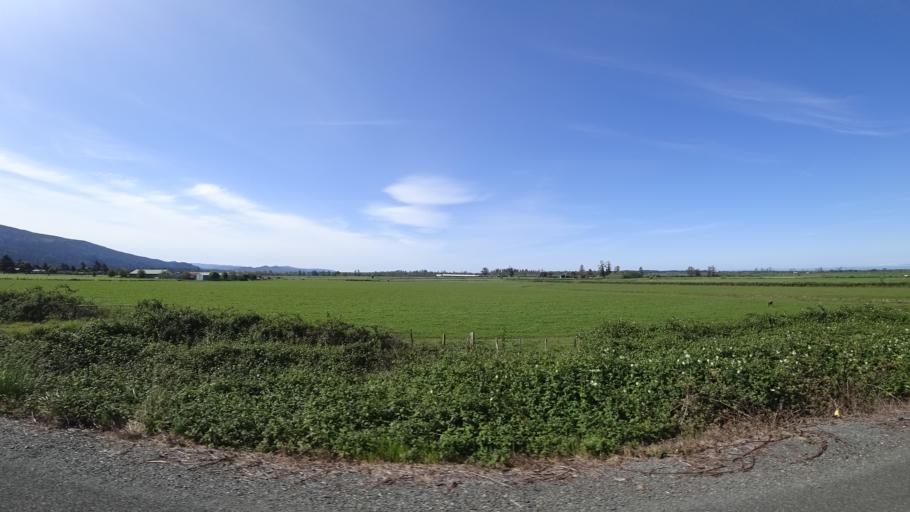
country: US
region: Oregon
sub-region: Curry County
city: Harbor
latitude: 41.9330
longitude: -124.1601
